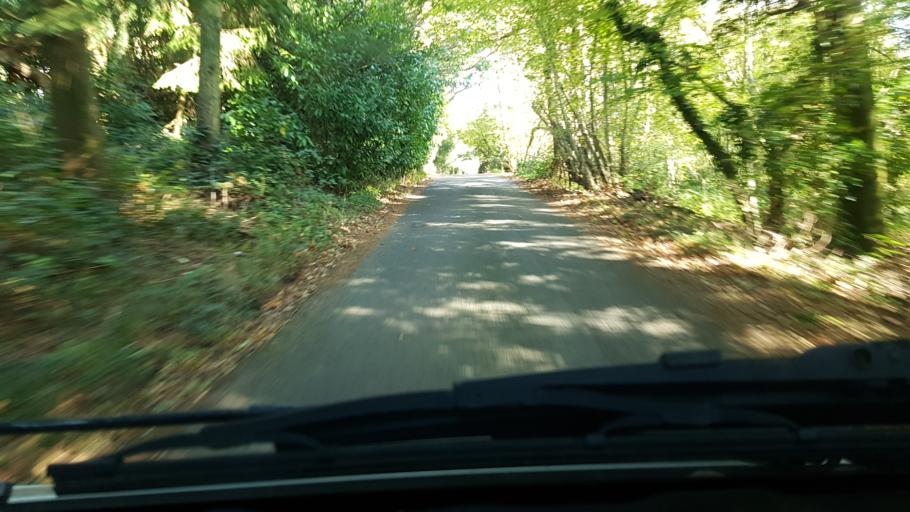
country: GB
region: England
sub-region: Surrey
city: Ockley
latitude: 51.1750
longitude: -0.3567
